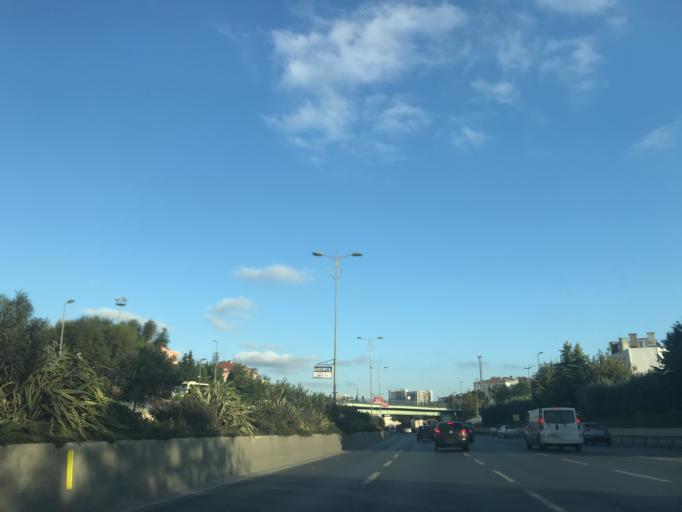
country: TR
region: Istanbul
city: Esenler
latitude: 41.0486
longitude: 28.8756
